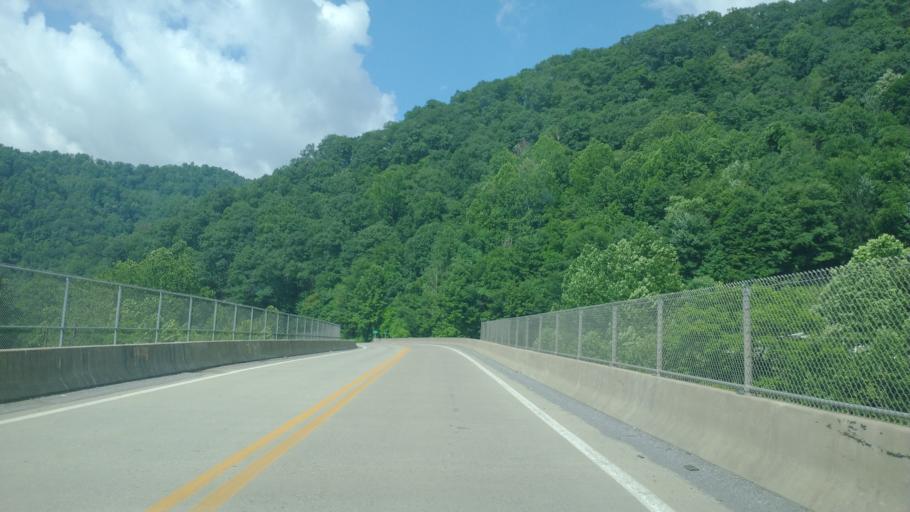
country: US
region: West Virginia
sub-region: McDowell County
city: Welch
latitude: 37.4086
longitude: -81.4614
